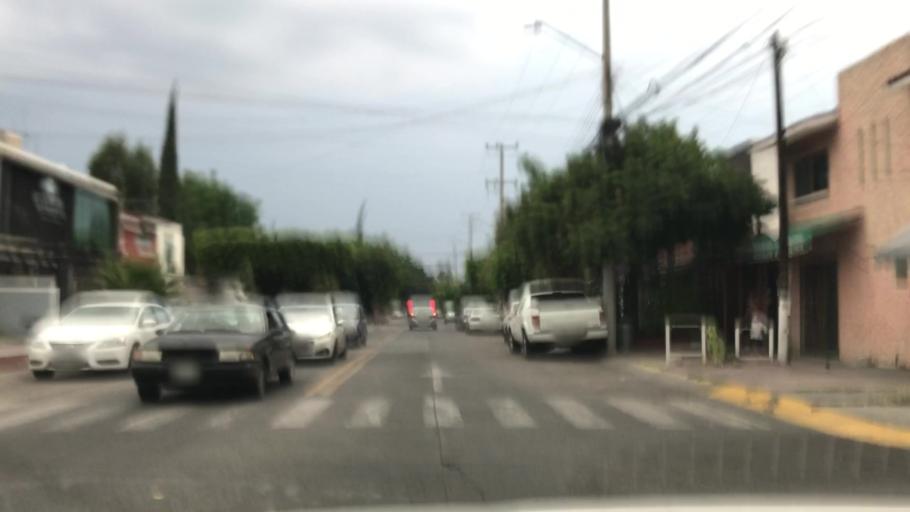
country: MX
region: Jalisco
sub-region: Tlajomulco de Zuniga
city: Palomar
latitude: 20.6322
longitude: -103.4304
